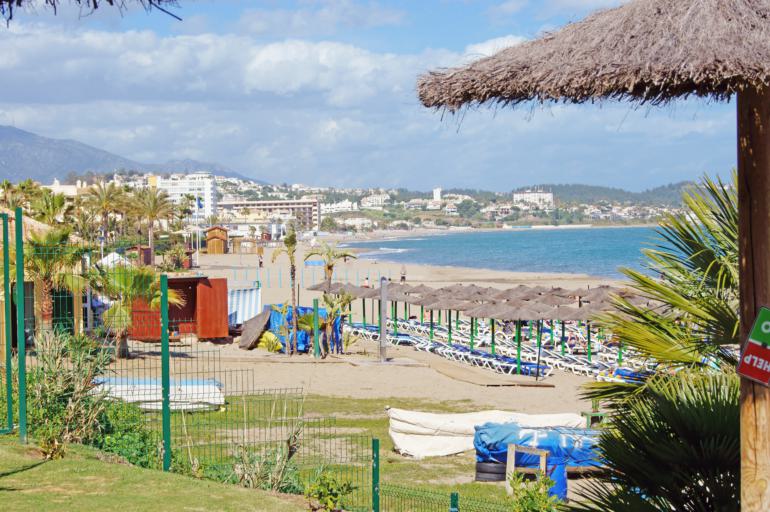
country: ES
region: Andalusia
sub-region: Provincia de Malaga
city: Fuengirola
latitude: 36.4938
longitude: -4.6907
